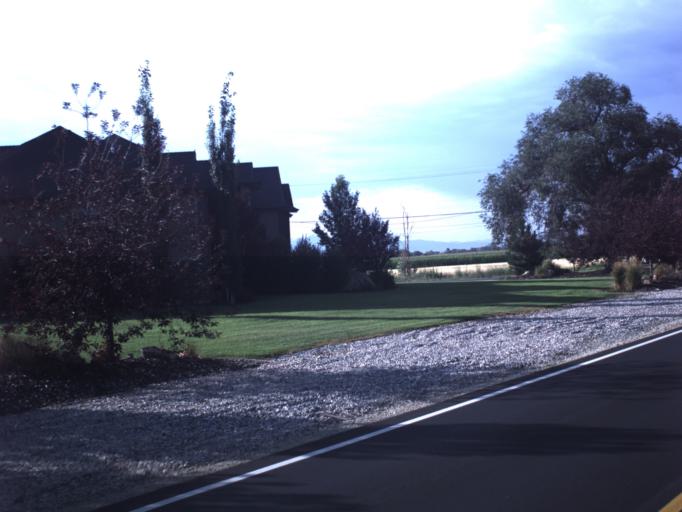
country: US
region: Utah
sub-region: Weber County
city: West Haven
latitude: 41.2352
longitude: -112.0928
